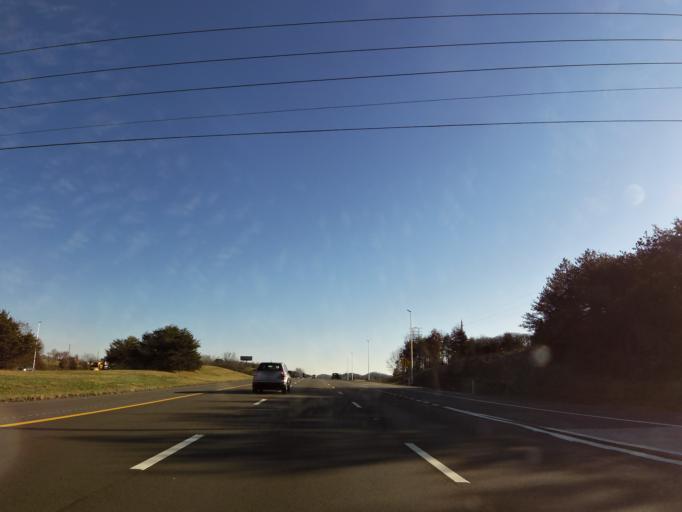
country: US
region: Tennessee
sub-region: Sevier County
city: Sevierville
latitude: 35.9839
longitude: -83.6035
